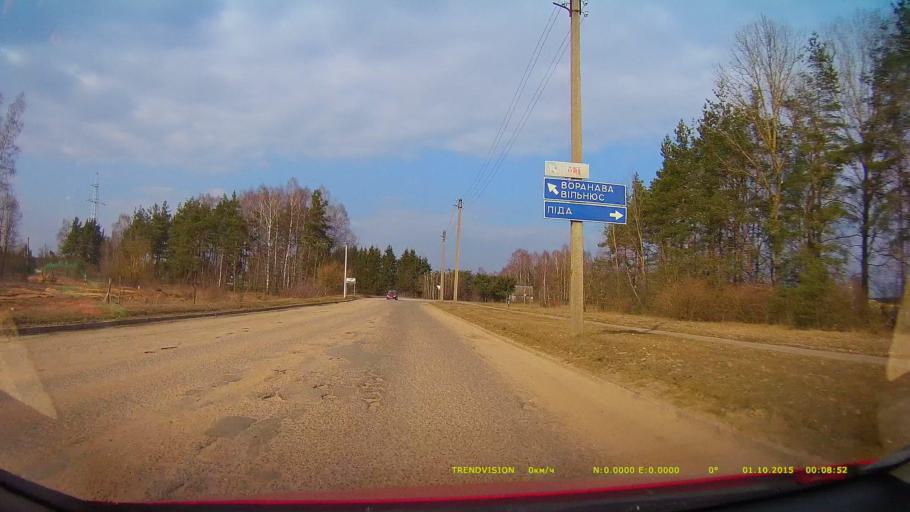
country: BY
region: Grodnenskaya
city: Lida
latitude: 53.9360
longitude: 25.2606
